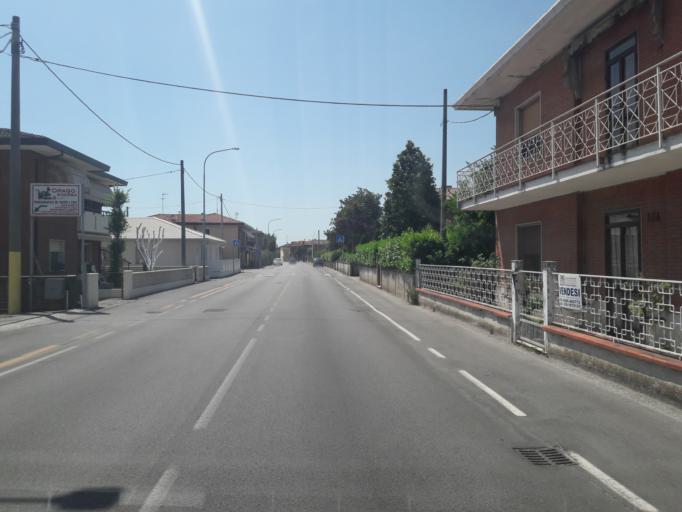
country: IT
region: Veneto
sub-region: Provincia di Rovigo
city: Taglio di Po
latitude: 45.0022
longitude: 12.2105
